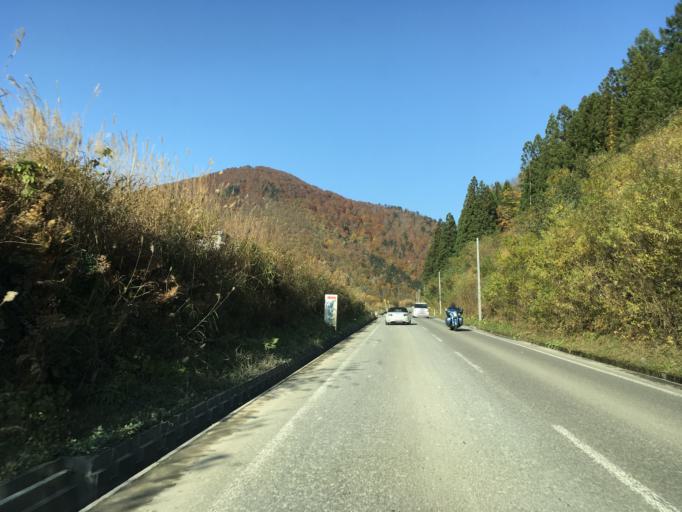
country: JP
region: Akita
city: Yuzawa
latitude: 39.0322
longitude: 140.7288
